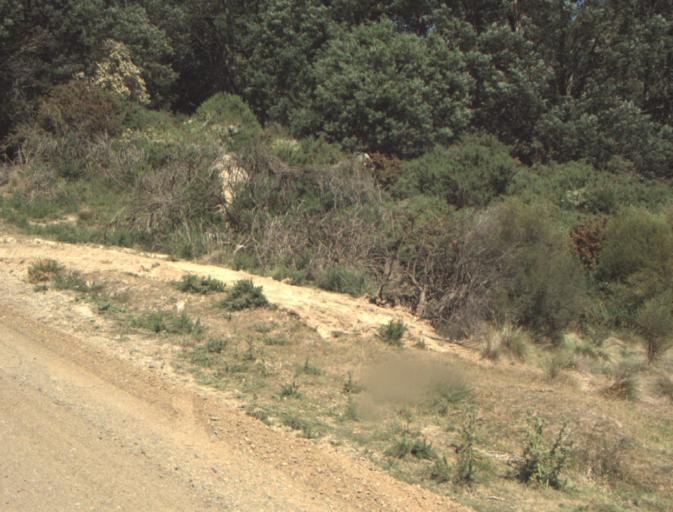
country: AU
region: Tasmania
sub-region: Dorset
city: Scottsdale
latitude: -41.3221
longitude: 147.4640
